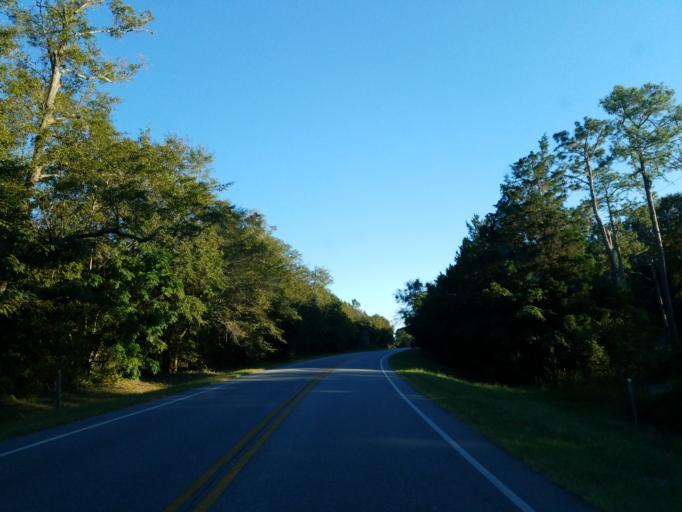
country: US
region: Georgia
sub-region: Worth County
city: Sylvester
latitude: 31.5766
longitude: -83.8551
